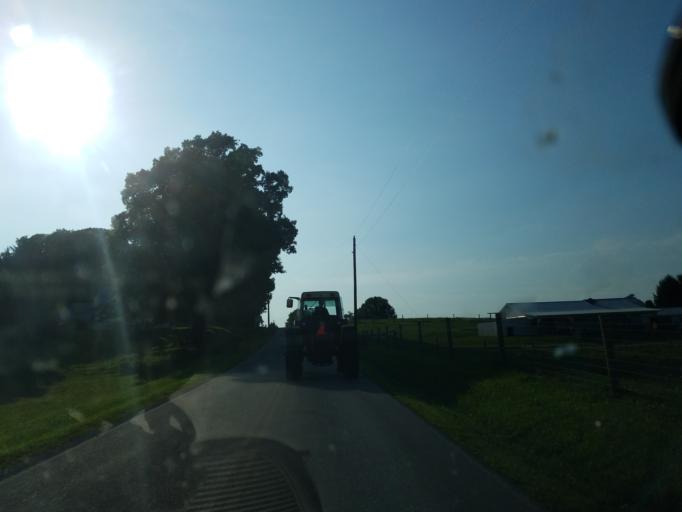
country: US
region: Ohio
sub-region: Adams County
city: West Union
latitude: 38.8865
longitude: -83.5072
